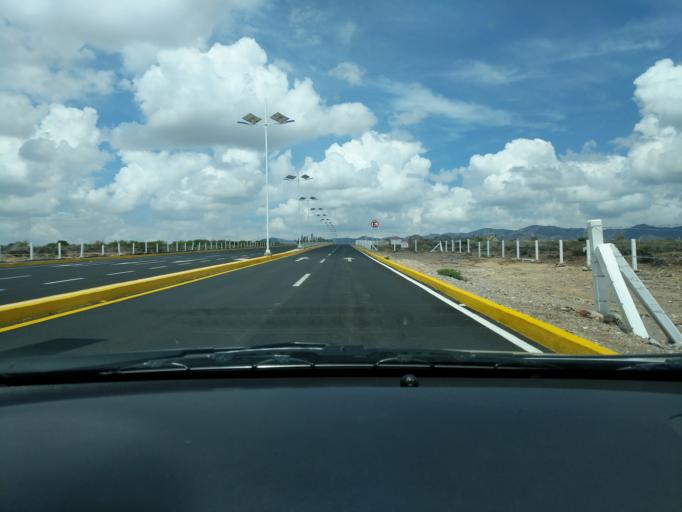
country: MX
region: San Luis Potosi
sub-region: Mexquitic de Carmona
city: Guadalupe Victoria
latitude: 22.1656
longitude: -101.0531
